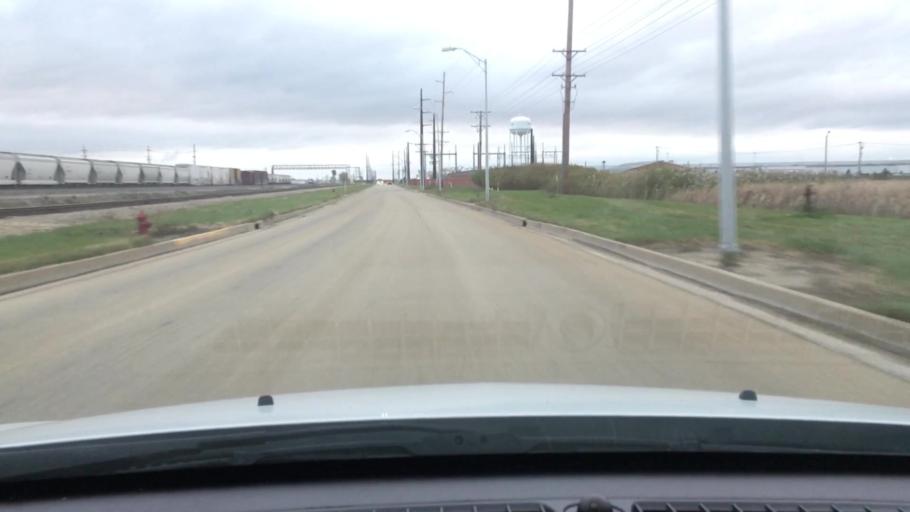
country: US
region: Illinois
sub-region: Ogle County
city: Rochelle
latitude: 41.9028
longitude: -89.0444
